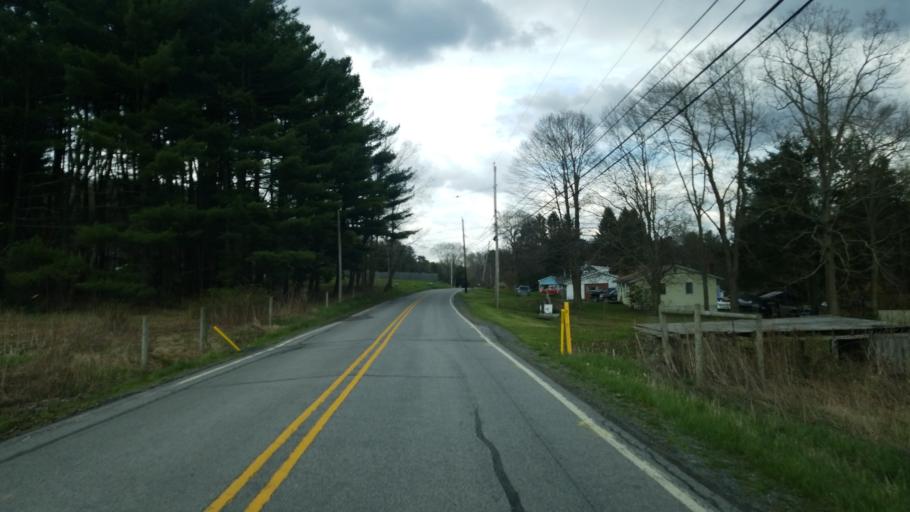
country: US
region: Pennsylvania
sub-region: Clearfield County
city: Curwensville
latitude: 40.8947
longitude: -78.4764
